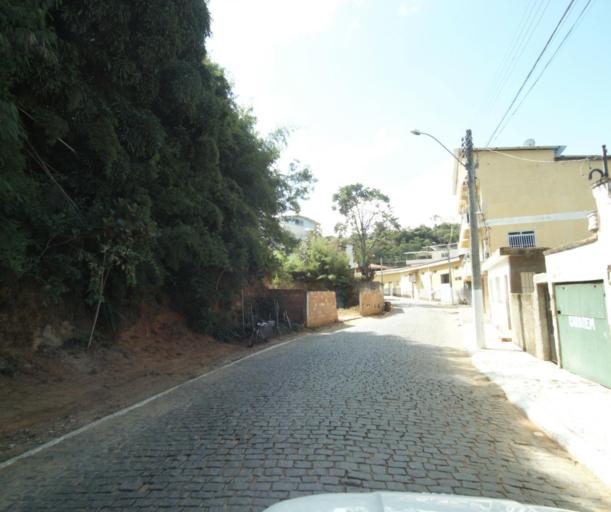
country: BR
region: Espirito Santo
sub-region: Sao Jose Do Calcado
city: Sao Jose do Calcado
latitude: -21.0262
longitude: -41.6526
